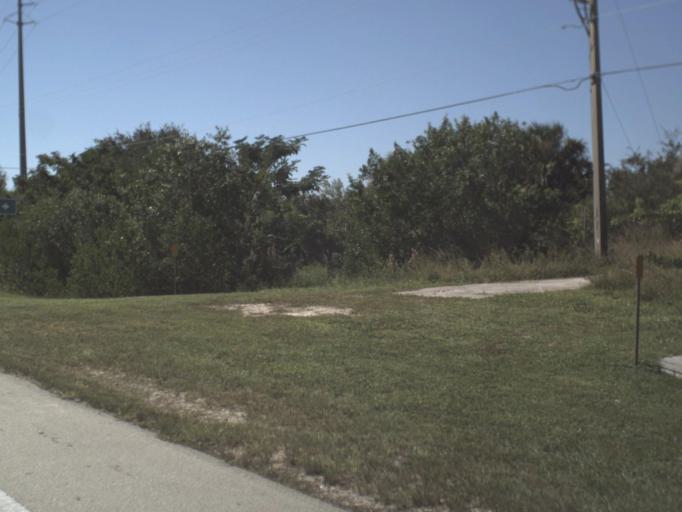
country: US
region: Florida
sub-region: Collier County
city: Marco
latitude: 25.9845
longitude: -81.7025
